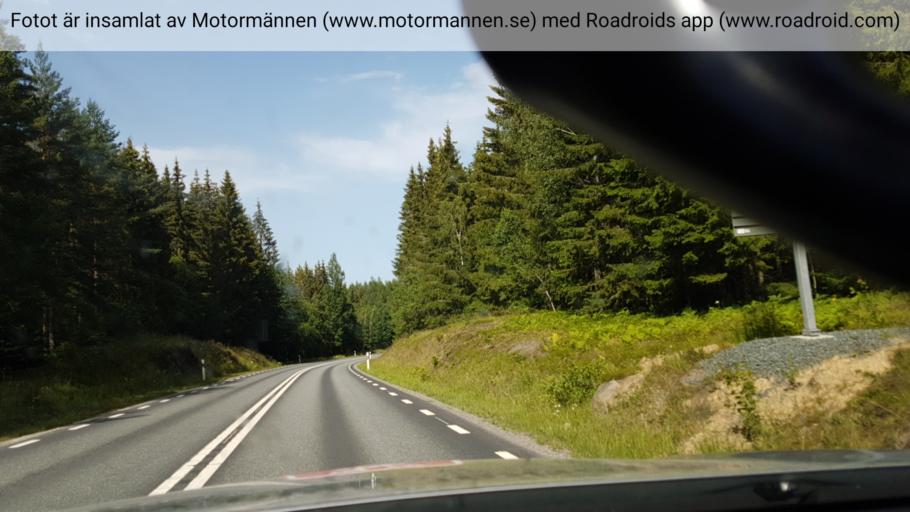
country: SE
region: Joenkoeping
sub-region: Aneby Kommun
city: Aneby
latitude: 57.8706
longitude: 14.8694
